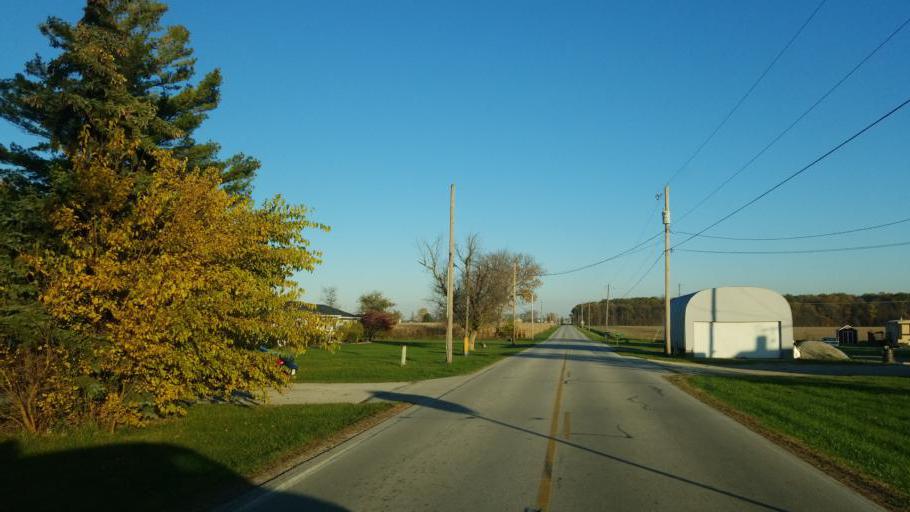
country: US
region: Ohio
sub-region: Sandusky County
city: Green Springs
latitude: 41.3068
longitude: -83.0532
